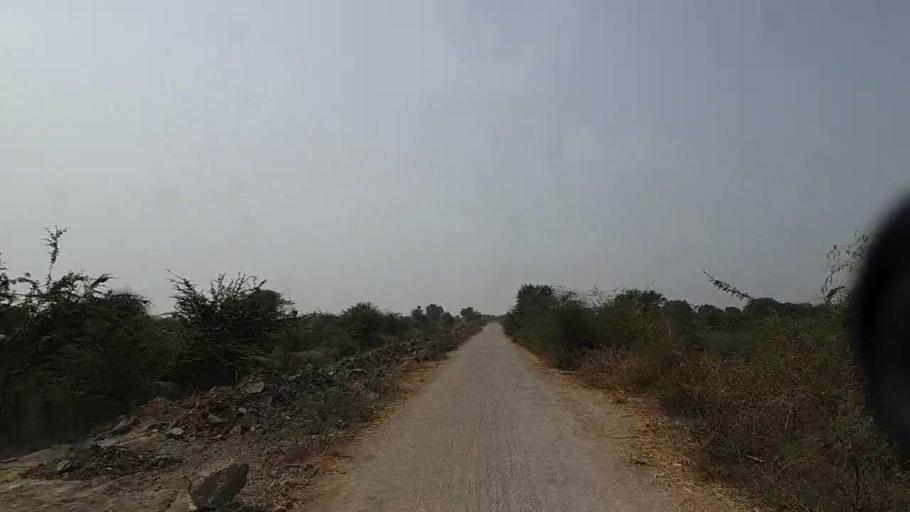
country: PK
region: Sindh
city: Naukot
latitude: 24.7725
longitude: 69.3107
